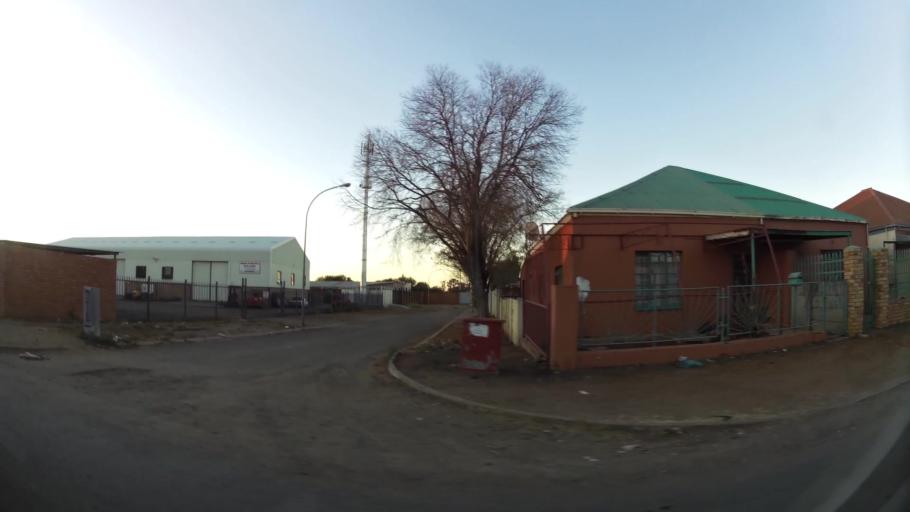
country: ZA
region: Northern Cape
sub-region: Frances Baard District Municipality
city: Kimberley
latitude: -28.7305
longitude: 24.7756
